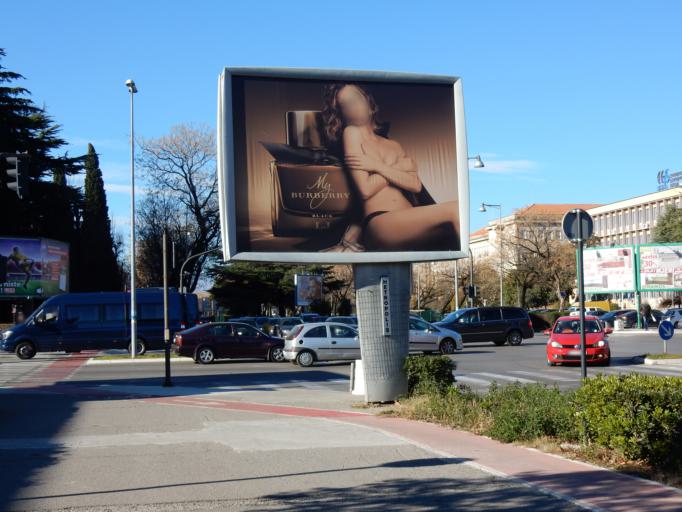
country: ME
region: Podgorica
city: Podgorica
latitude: 42.4405
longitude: 19.2551
